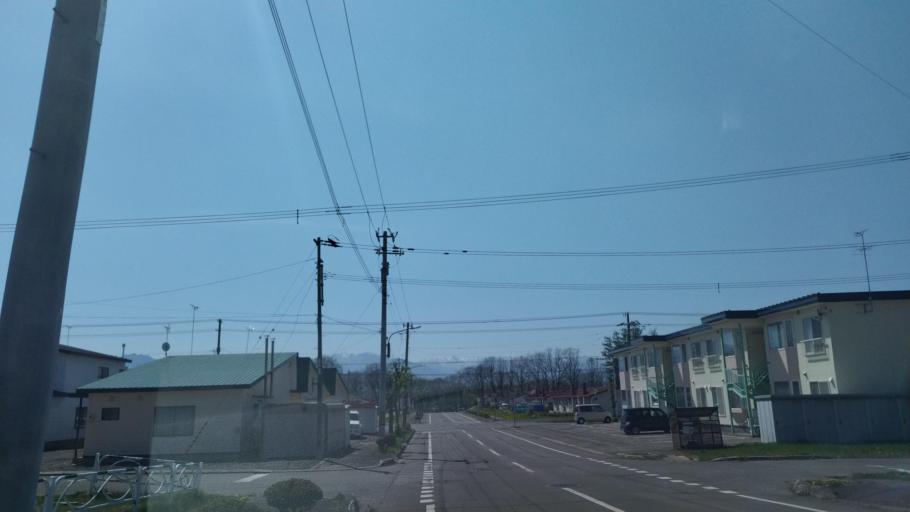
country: JP
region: Hokkaido
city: Obihiro
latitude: 42.9114
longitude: 143.0441
